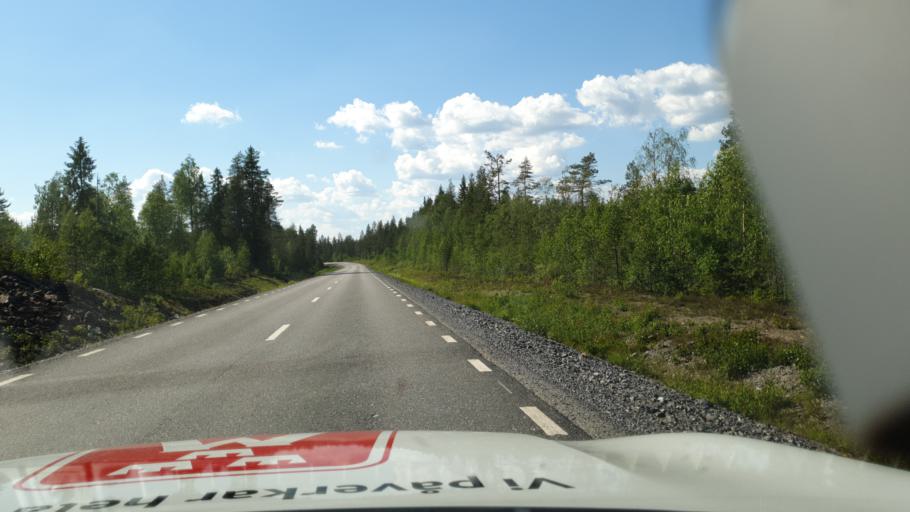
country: SE
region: Vaesterbotten
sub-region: Vindelns Kommun
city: Vindeln
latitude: 64.2493
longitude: 20.0543
